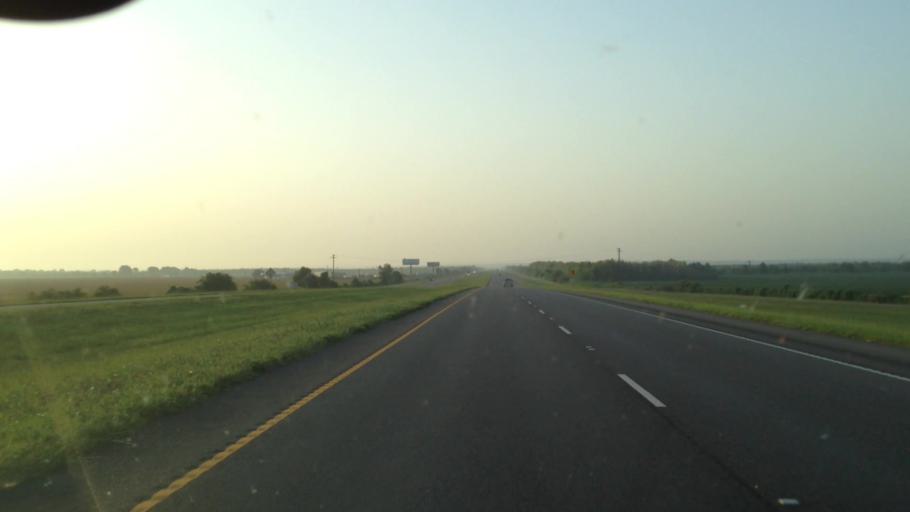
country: US
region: Louisiana
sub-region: Natchitoches Parish
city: Campti
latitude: 31.8377
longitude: -93.2759
